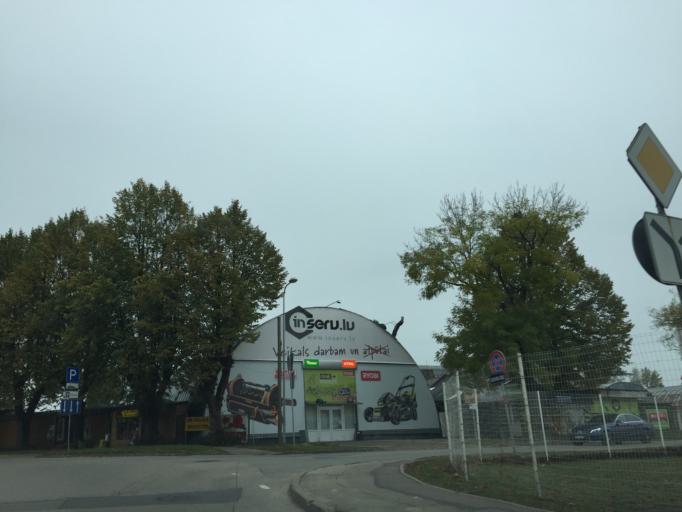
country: LV
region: Marupe
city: Marupe
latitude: 56.9284
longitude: 24.0385
